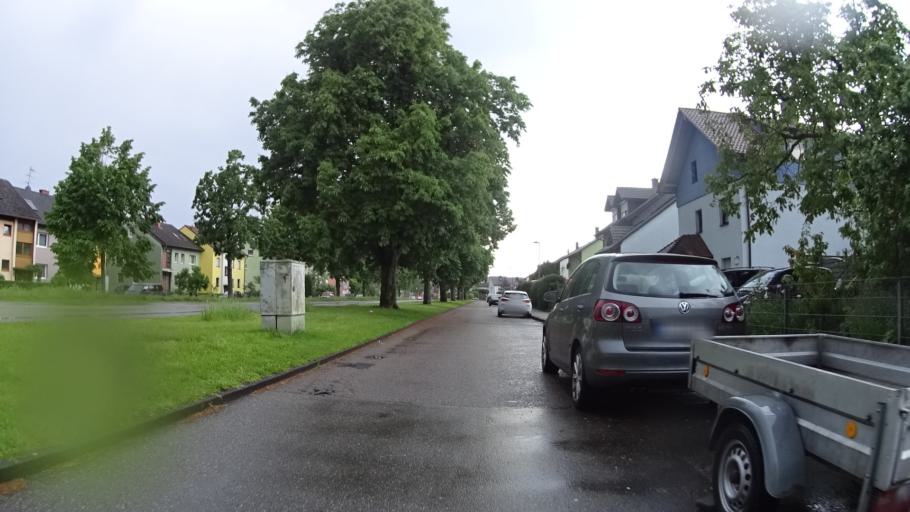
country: DE
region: Baden-Wuerttemberg
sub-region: Karlsruhe Region
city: Durmersheim
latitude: 48.9410
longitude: 8.2762
